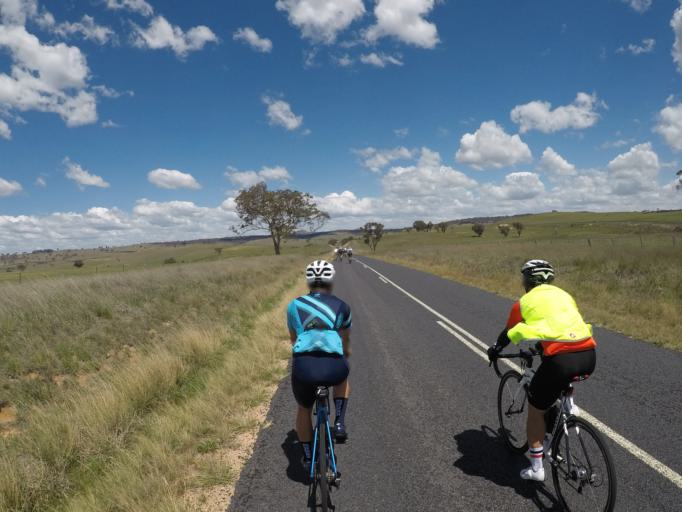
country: AU
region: New South Wales
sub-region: Bathurst Regional
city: Perthville
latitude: -33.5585
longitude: 149.4191
